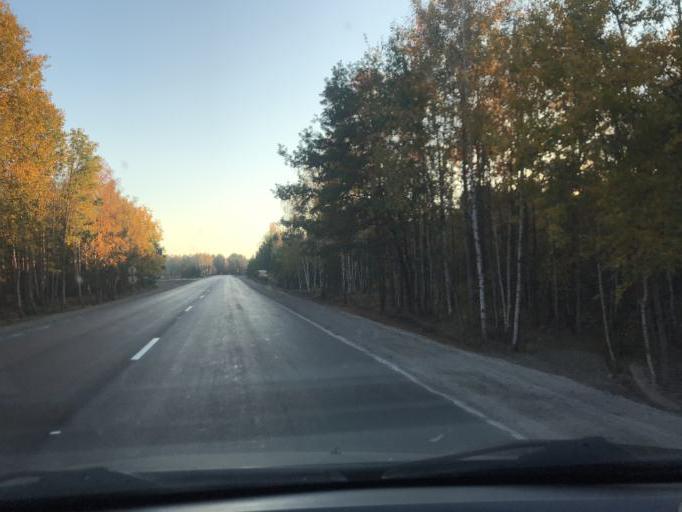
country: BY
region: Gomel
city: Brahin
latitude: 51.8632
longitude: 30.3722
